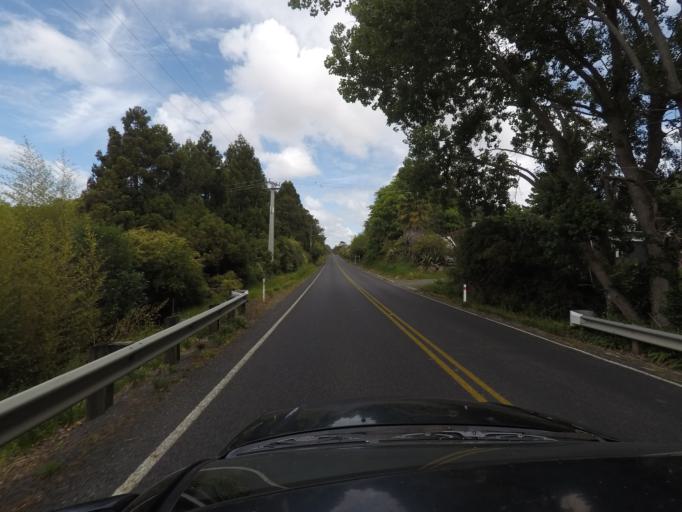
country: NZ
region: Auckland
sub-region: Auckland
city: Parakai
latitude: -36.6434
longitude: 174.5129
